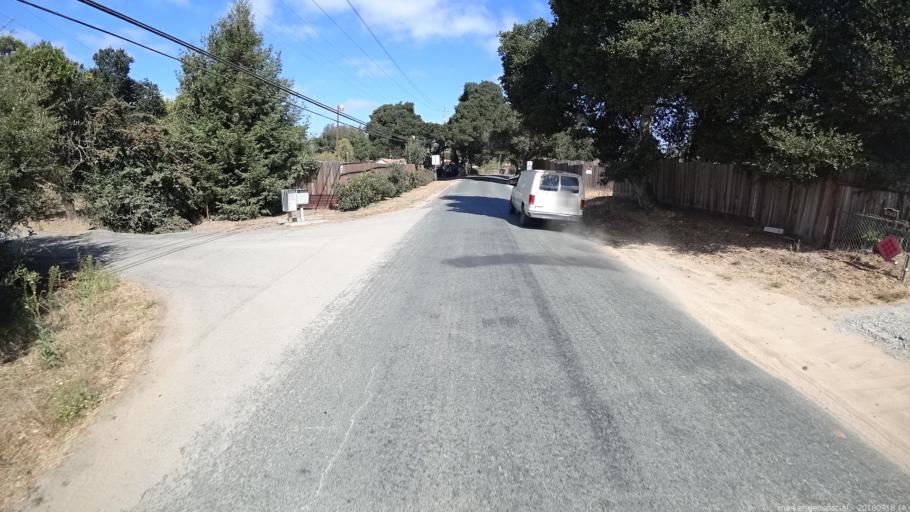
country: US
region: California
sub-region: Monterey County
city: Prunedale
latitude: 36.7775
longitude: -121.6717
